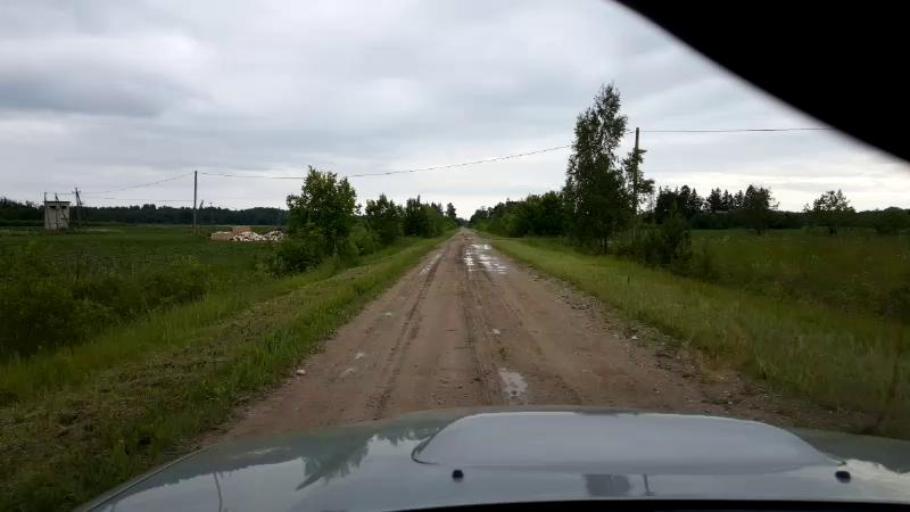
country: EE
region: Paernumaa
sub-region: Halinga vald
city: Parnu-Jaagupi
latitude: 58.5606
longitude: 24.5764
